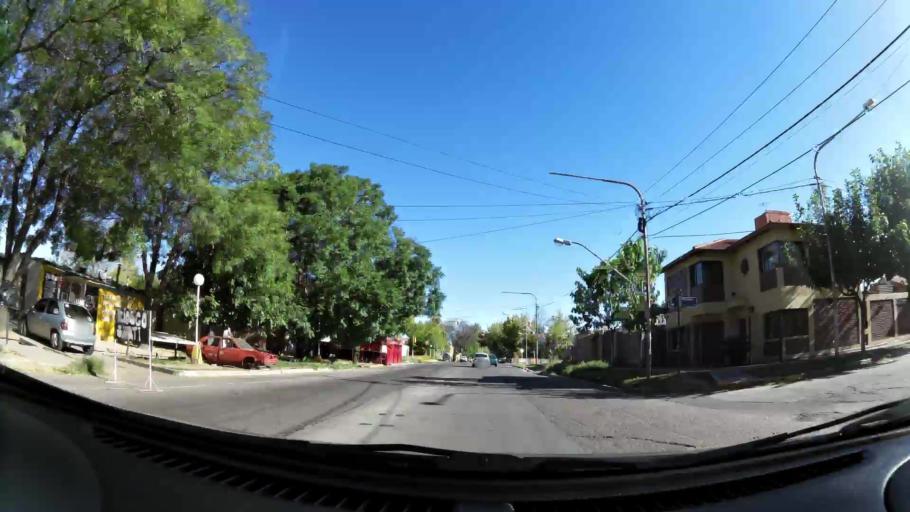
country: AR
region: Mendoza
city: Las Heras
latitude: -32.8615
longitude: -68.8280
